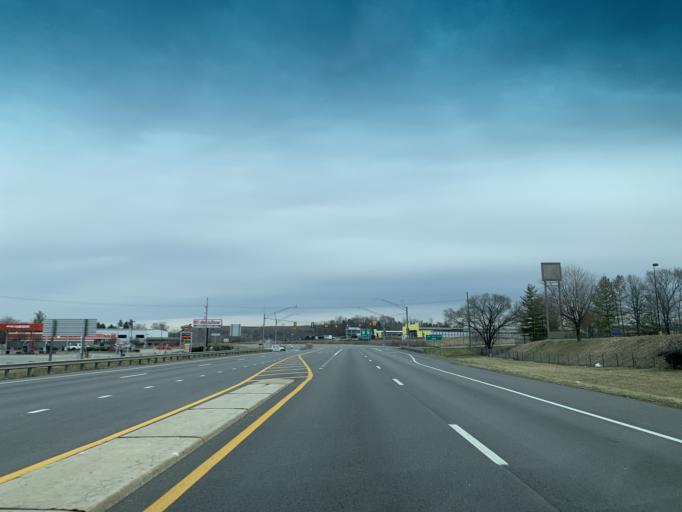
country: US
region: West Virginia
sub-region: Berkeley County
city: Martinsburg
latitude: 39.4411
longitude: -77.9799
